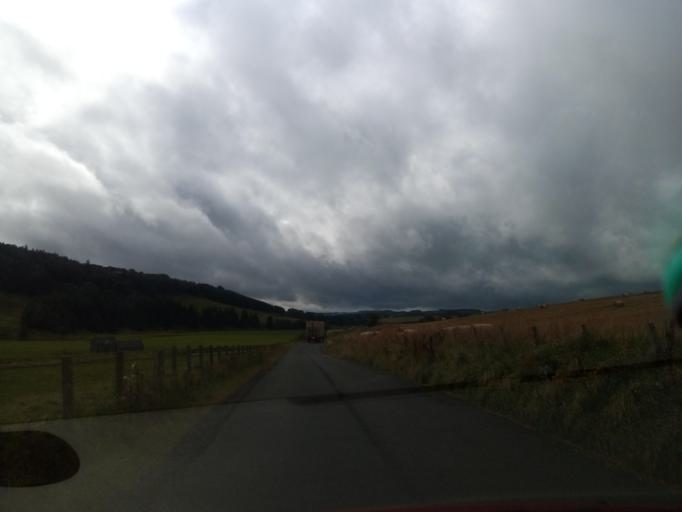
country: GB
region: Scotland
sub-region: The Scottish Borders
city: Duns
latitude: 55.8299
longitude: -2.4475
